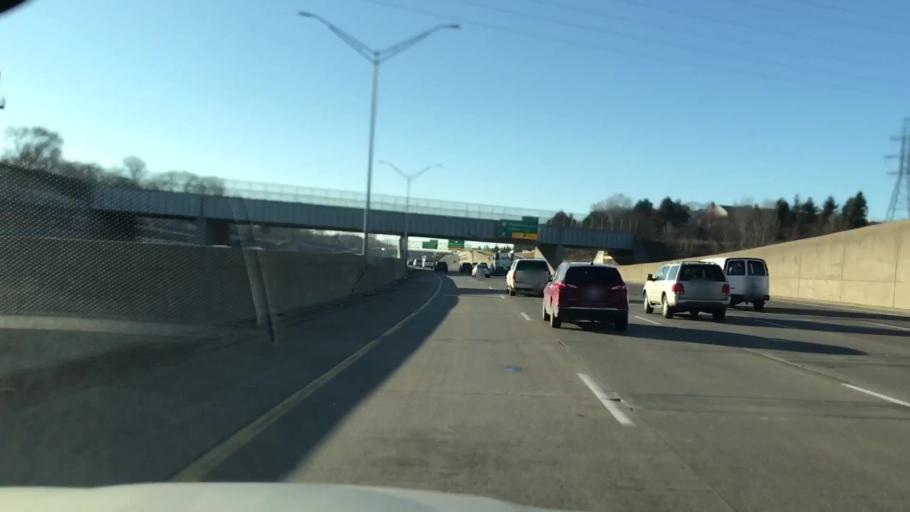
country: US
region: Michigan
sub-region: Oakland County
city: Pleasant Ridge
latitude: 42.4769
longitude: -83.1355
